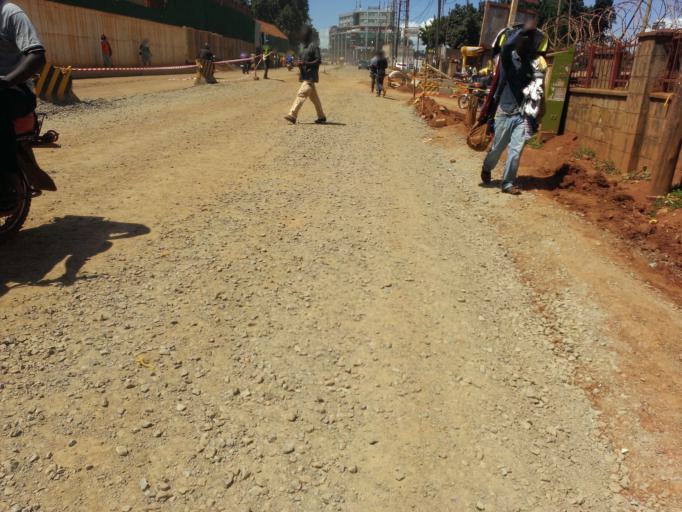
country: UG
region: Central Region
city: Kampala Central Division
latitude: 0.3276
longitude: 32.5672
